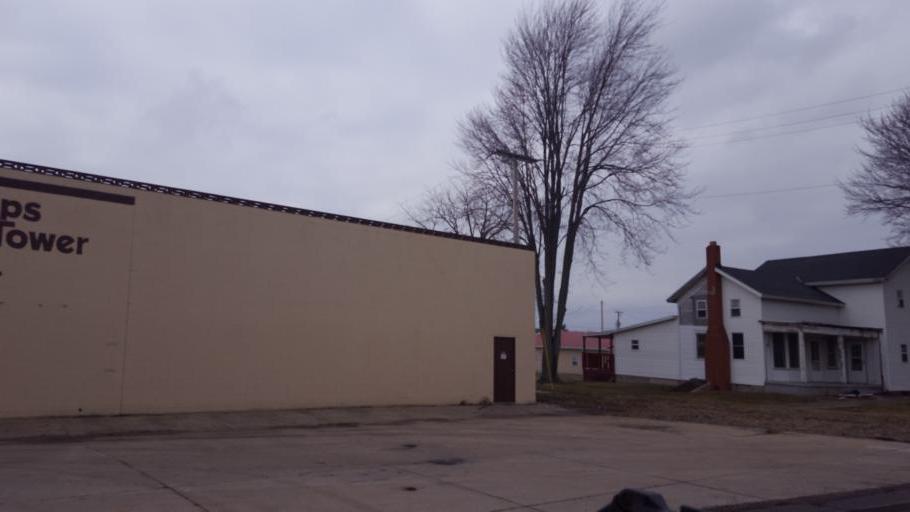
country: US
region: Ohio
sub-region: Richland County
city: Shelby
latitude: 40.9076
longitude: -82.6590
